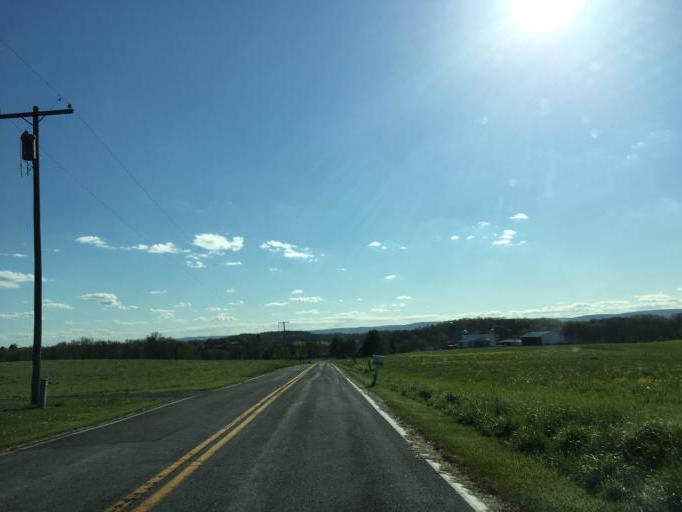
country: US
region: Maryland
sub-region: Frederick County
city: Emmitsburg
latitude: 39.6527
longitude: -77.2835
